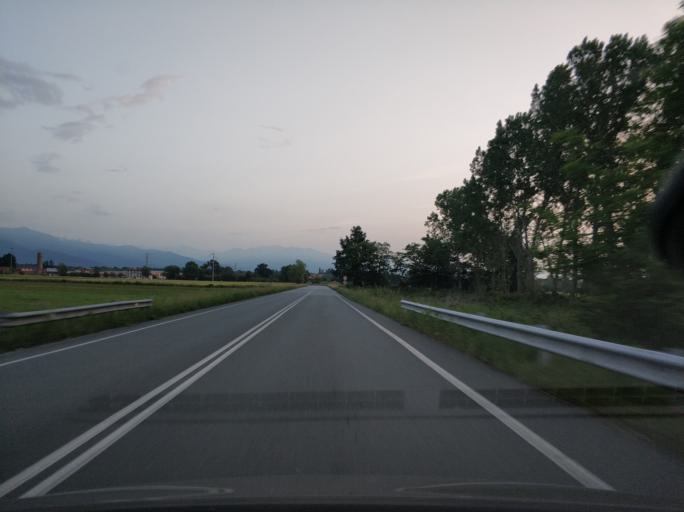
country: IT
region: Piedmont
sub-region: Provincia di Torino
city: San Maurizio
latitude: 45.2137
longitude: 7.6429
